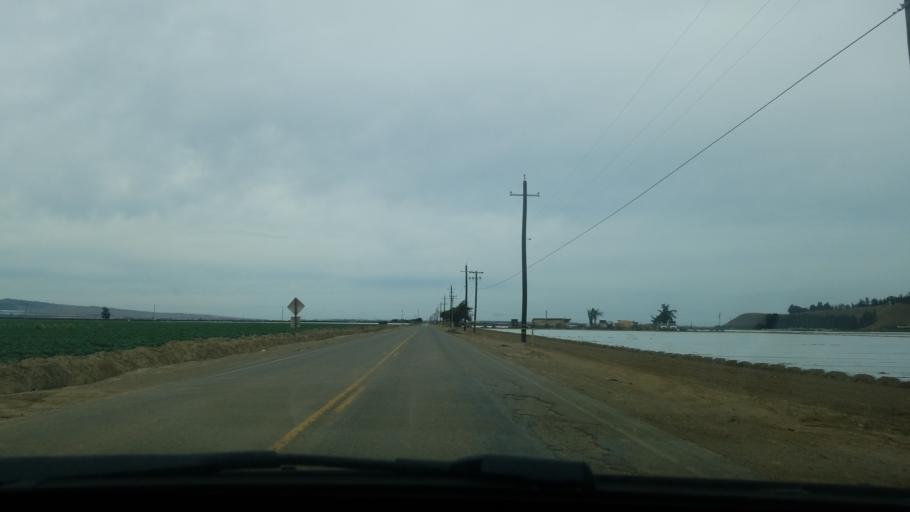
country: US
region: California
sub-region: San Luis Obispo County
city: Nipomo
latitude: 35.0062
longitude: -120.5047
